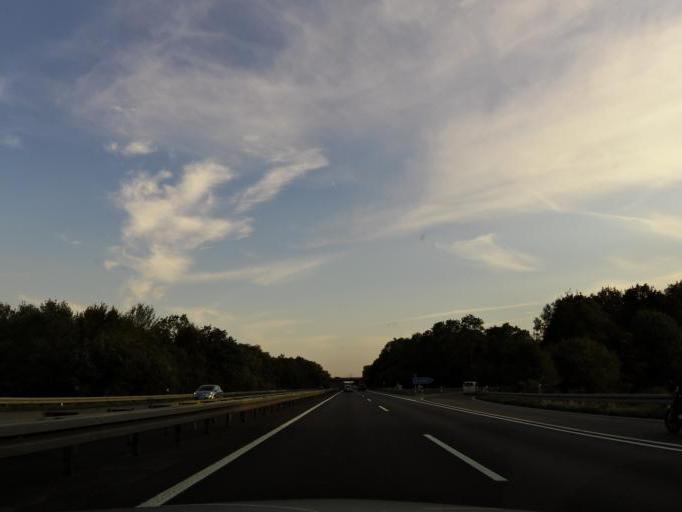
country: DE
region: Hesse
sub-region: Regierungsbezirk Darmstadt
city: Alsbach-Hahnlein
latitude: 49.7472
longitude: 8.5434
